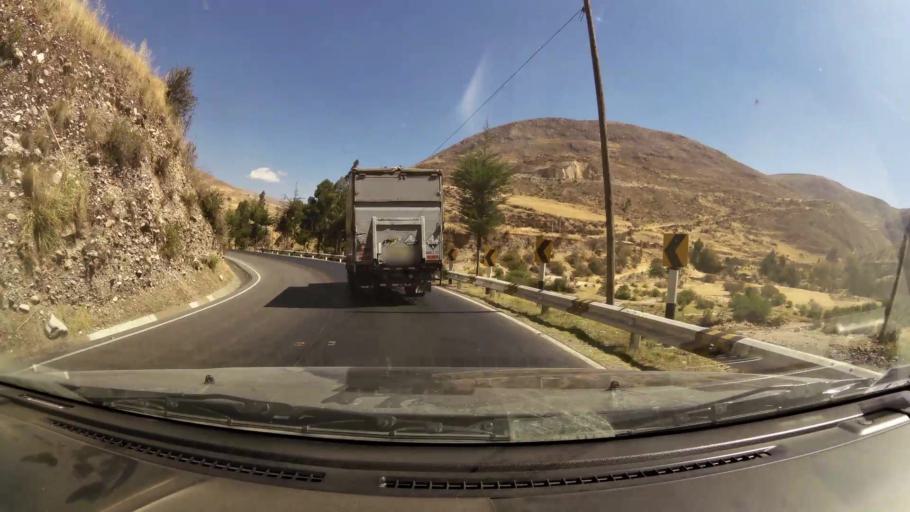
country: PE
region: Junin
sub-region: Provincia de Jauja
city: Parco
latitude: -11.7834
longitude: -75.5759
